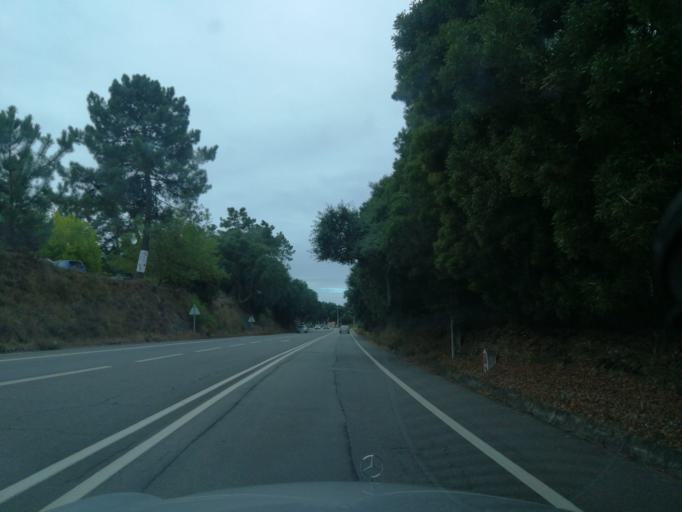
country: PT
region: Aveiro
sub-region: Agueda
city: Agueda
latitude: 40.5847
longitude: -8.4495
